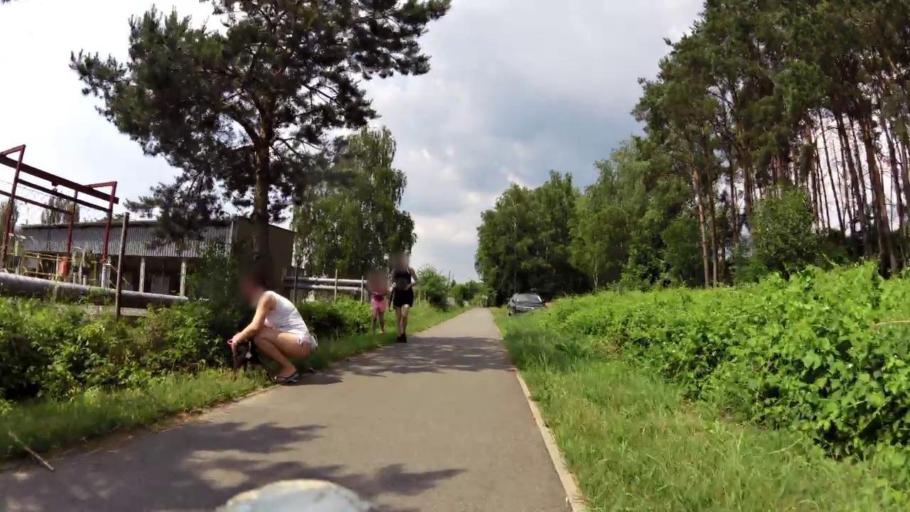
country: PL
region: Kujawsko-Pomorskie
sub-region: Powiat bydgoski
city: Koronowo
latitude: 53.3017
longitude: 17.9460
